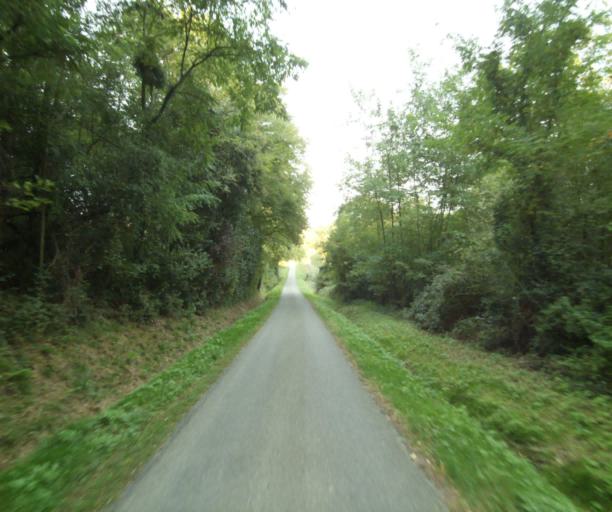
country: FR
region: Midi-Pyrenees
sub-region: Departement du Gers
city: Eauze
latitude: 43.8911
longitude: 0.0552
